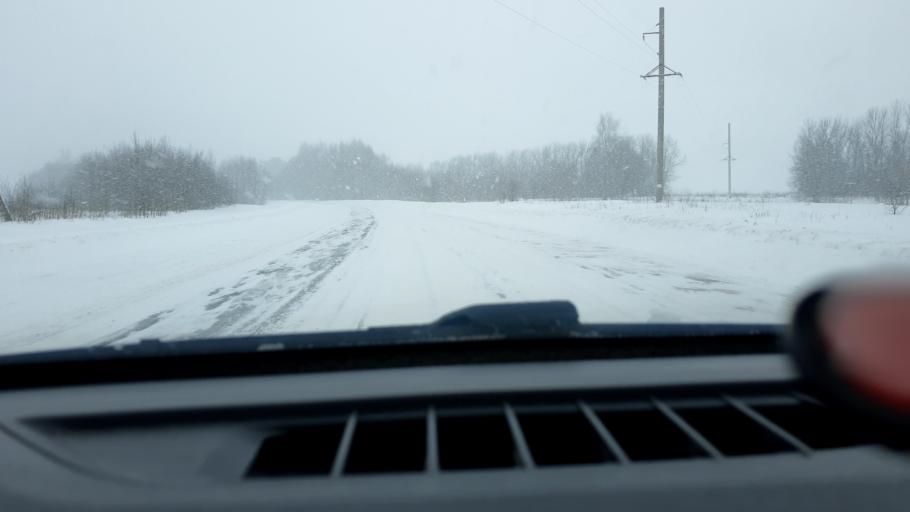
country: RU
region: Nizjnij Novgorod
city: Bol'shoye Murashkino
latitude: 55.7201
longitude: 44.7704
